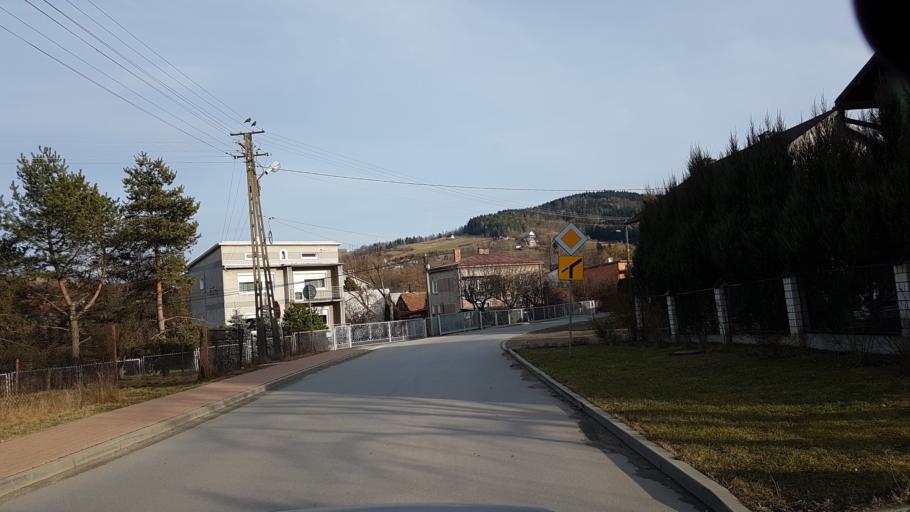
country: PL
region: Lesser Poland Voivodeship
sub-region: Powiat nowosadecki
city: Stary Sacz
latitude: 49.5405
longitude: 20.6526
